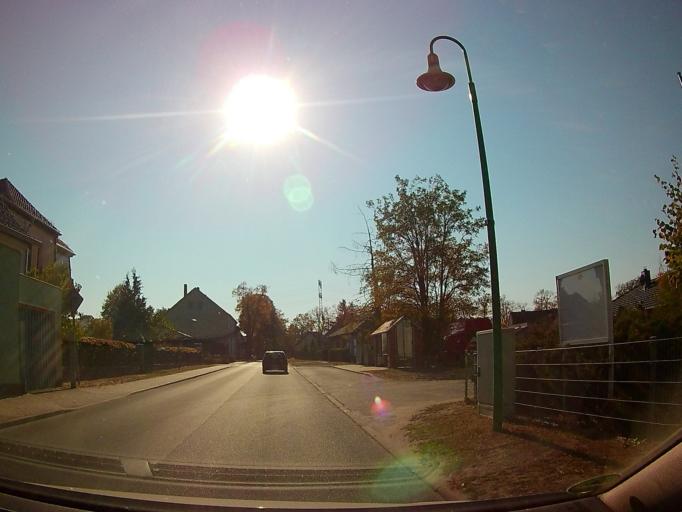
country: DE
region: Brandenburg
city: Baruth
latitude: 52.1314
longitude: 13.4979
